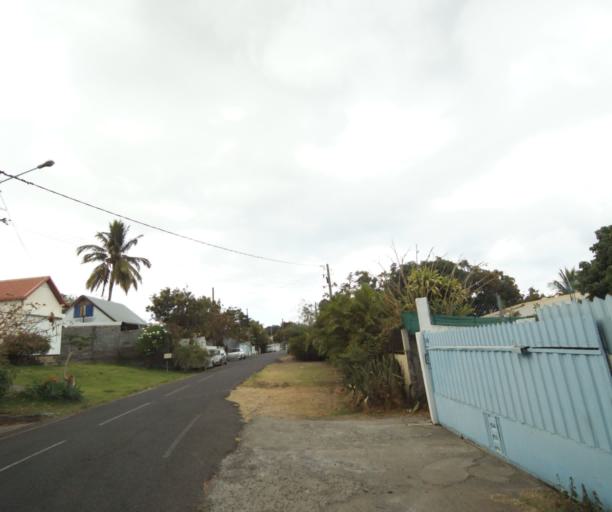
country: RE
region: Reunion
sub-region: Reunion
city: Saint-Paul
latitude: -21.0541
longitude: 55.2349
